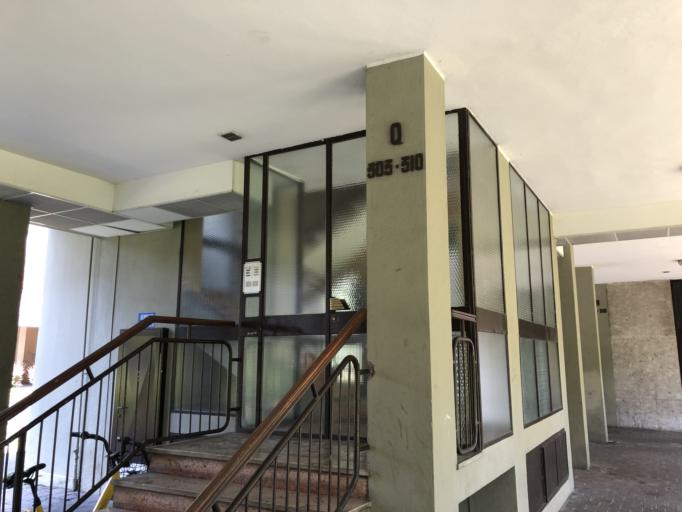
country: IT
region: Lombardy
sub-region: Citta metropolitana di Milano
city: Cormano
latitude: 45.5266
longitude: 9.1637
